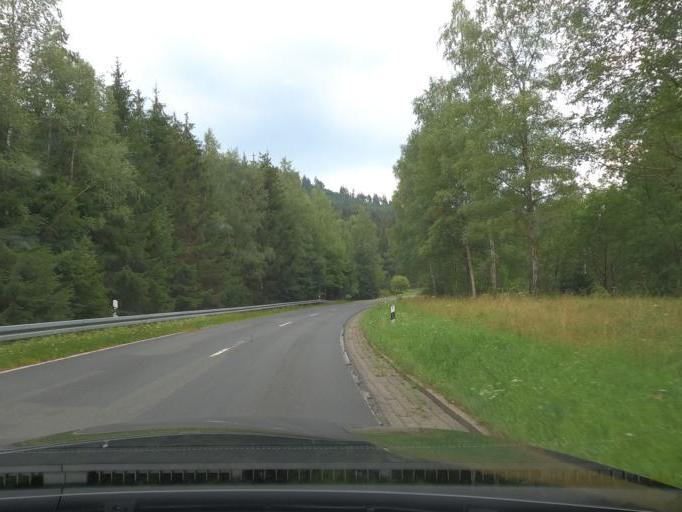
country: DE
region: Lower Saxony
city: Wildemann
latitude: 51.8532
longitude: 10.2749
